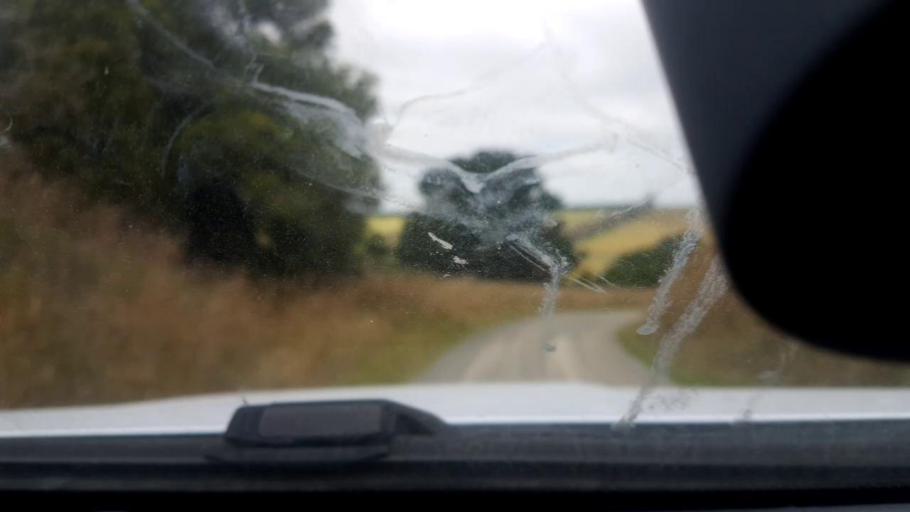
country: NZ
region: Canterbury
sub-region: Timaru District
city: Pleasant Point
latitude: -44.1611
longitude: 171.1457
